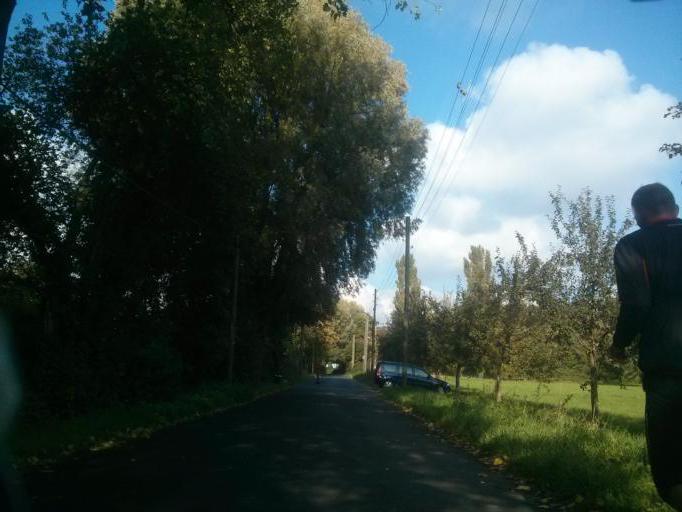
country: DE
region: North Rhine-Westphalia
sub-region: Regierungsbezirk Koln
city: Poll
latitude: 50.9073
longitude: 6.9879
